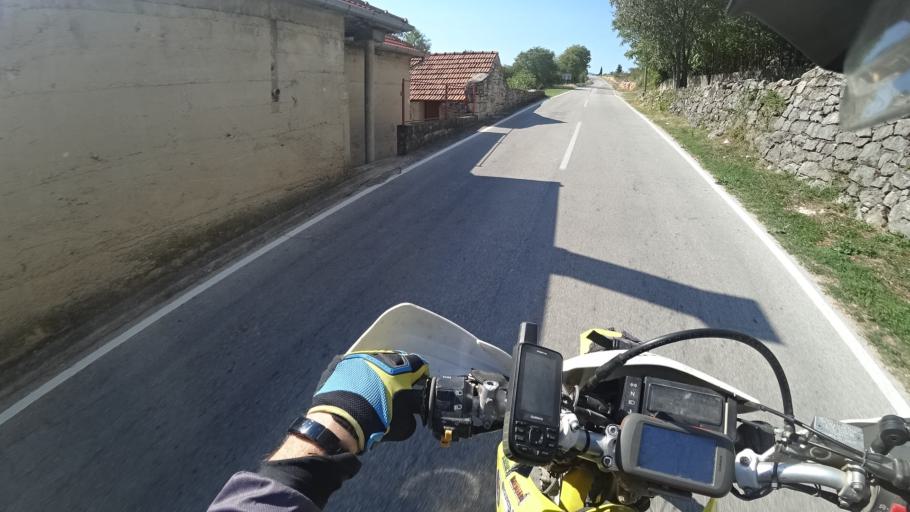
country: HR
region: Sibensko-Kniniska
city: Knin
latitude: 44.0122
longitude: 16.1967
